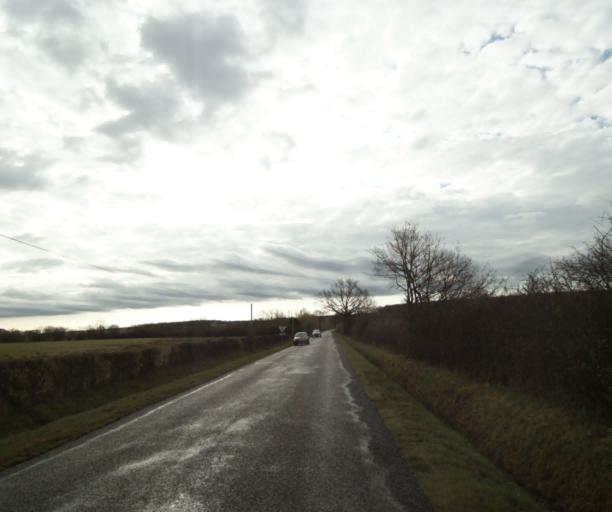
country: FR
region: Auvergne
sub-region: Departement de l'Allier
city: Toulon-sur-Allier
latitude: 46.5352
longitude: 3.4008
